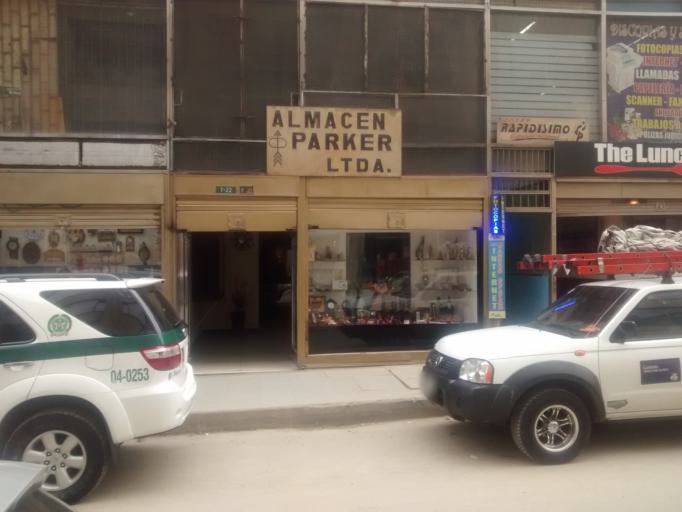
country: CO
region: Bogota D.C.
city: Bogota
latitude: 4.6003
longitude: -74.0746
